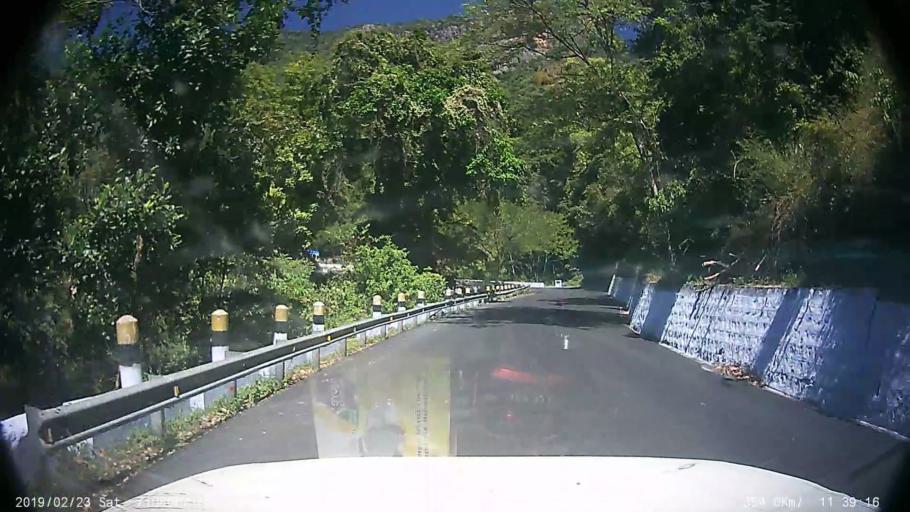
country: IN
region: Tamil Nadu
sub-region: Nilgiri
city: Wellington
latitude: 11.3395
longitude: 76.8419
